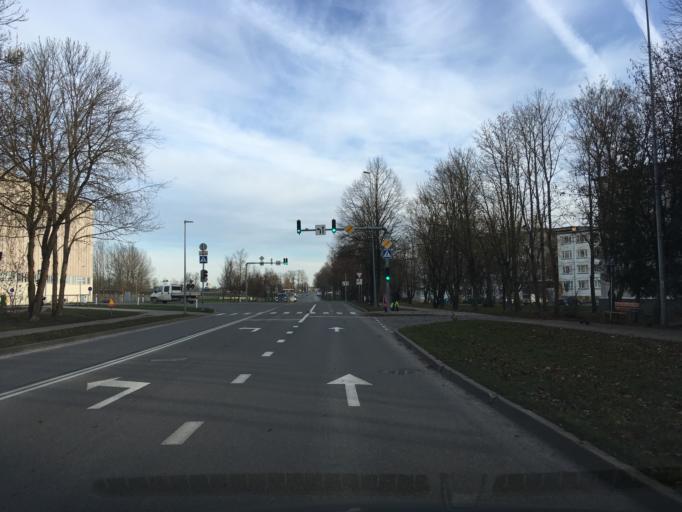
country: EE
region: Ida-Virumaa
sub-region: Johvi vald
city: Johvi
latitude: 59.3515
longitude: 27.4133
